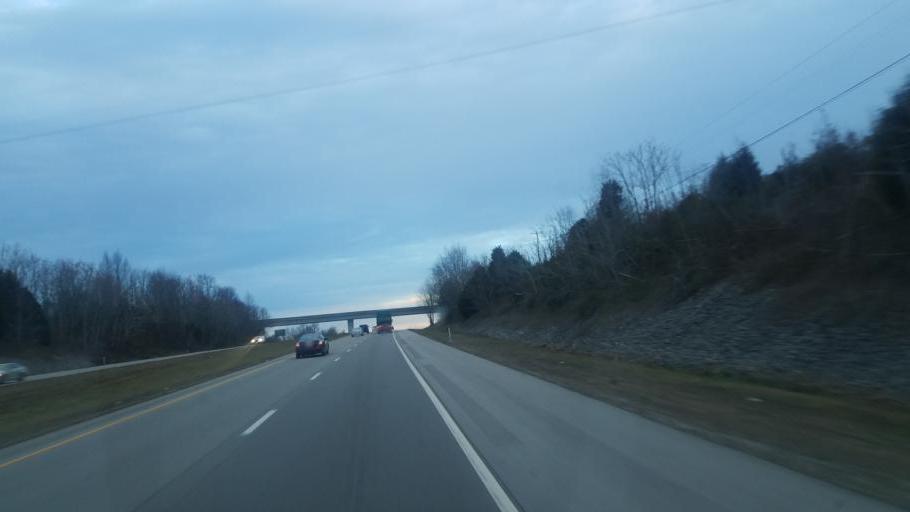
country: US
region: Tennessee
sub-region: Putnam County
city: Cookeville
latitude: 36.0711
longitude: -85.5072
